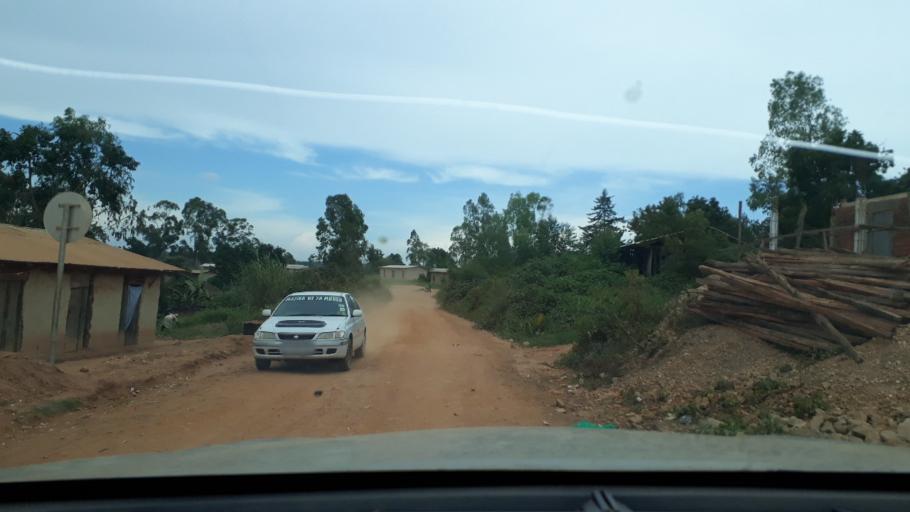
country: CD
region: Eastern Province
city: Bunia
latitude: 1.8603
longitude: 30.4792
